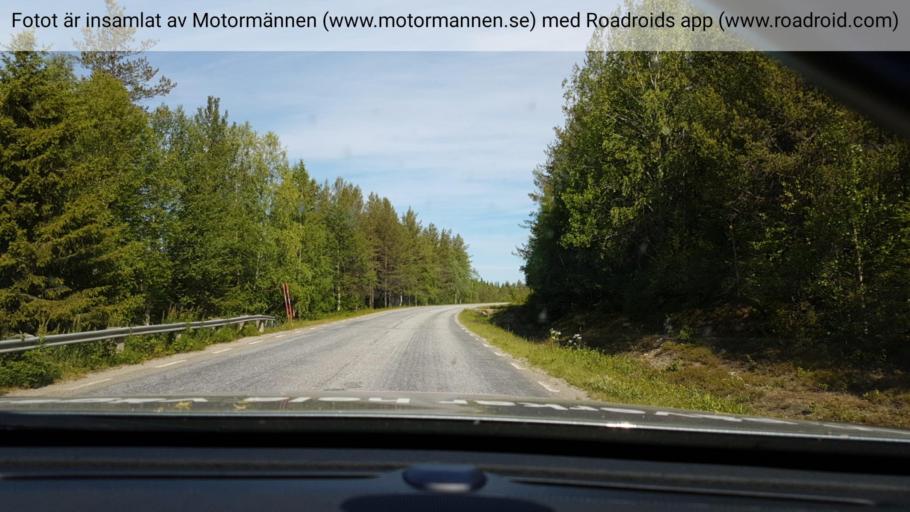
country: SE
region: Vaesterbotten
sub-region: Vilhelmina Kommun
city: Sjoberg
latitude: 64.4890
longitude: 15.9411
